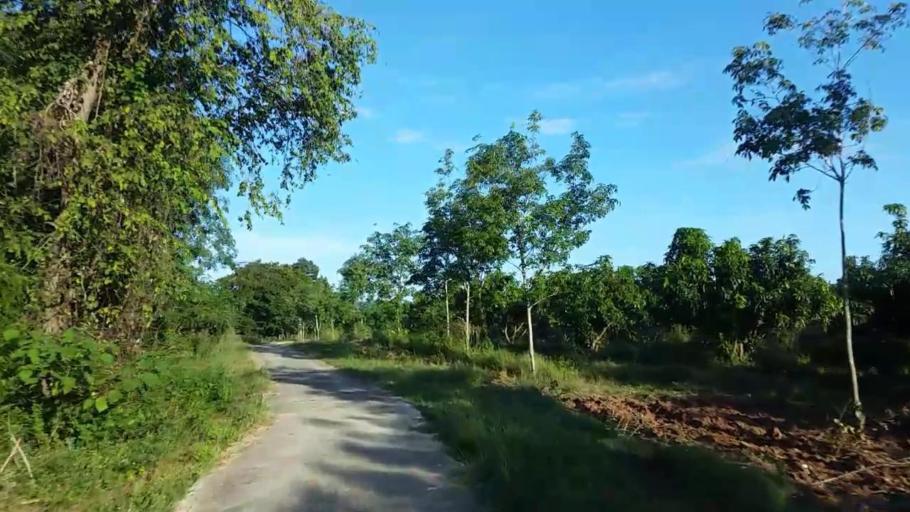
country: TH
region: Chaiyaphum
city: Thep Sathit
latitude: 15.5492
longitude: 101.4766
